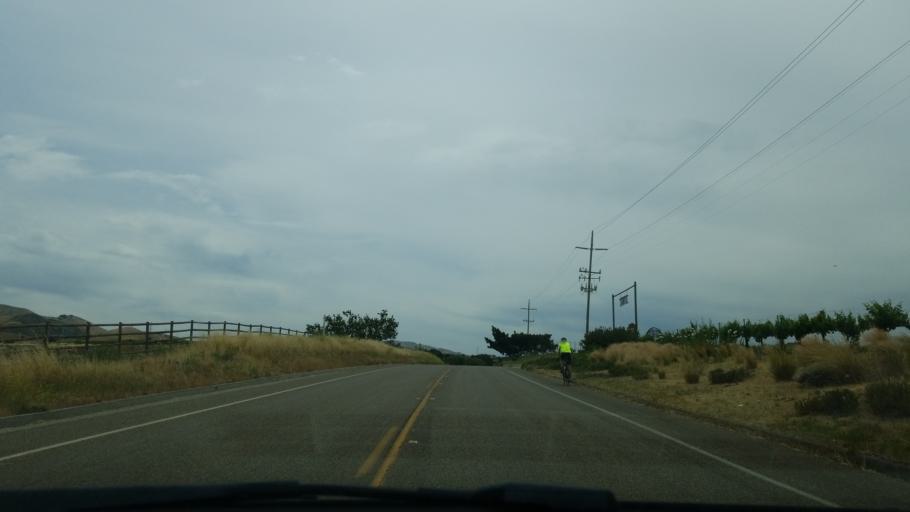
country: US
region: California
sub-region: San Luis Obispo County
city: Arroyo Grande
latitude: 35.2006
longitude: -120.5715
